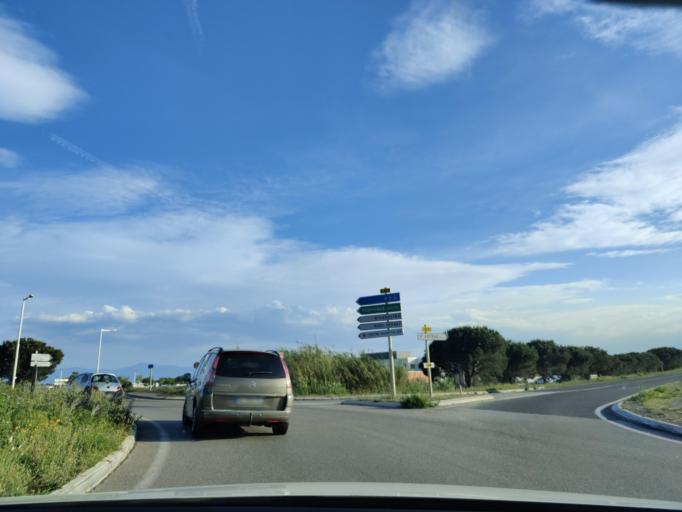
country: FR
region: Languedoc-Roussillon
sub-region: Departement des Pyrenees-Orientales
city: Peyrestortes
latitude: 42.7292
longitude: 2.8768
